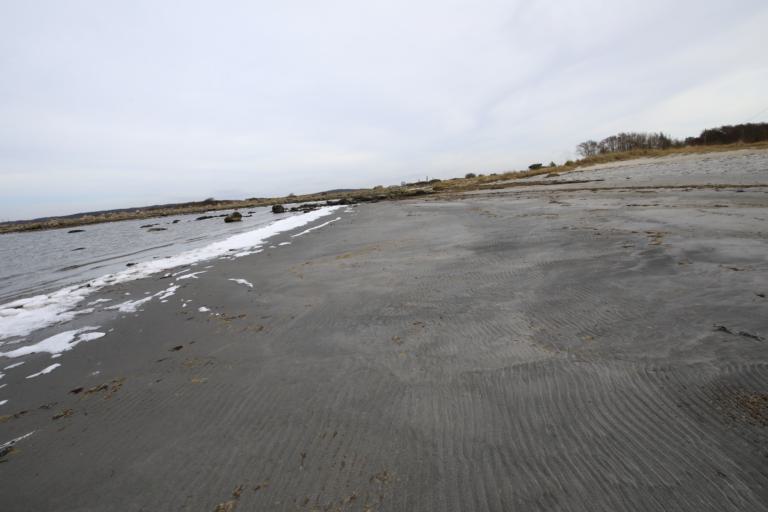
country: SE
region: Halland
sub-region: Kungsbacka Kommun
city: Frillesas
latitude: 57.2404
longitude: 12.1018
